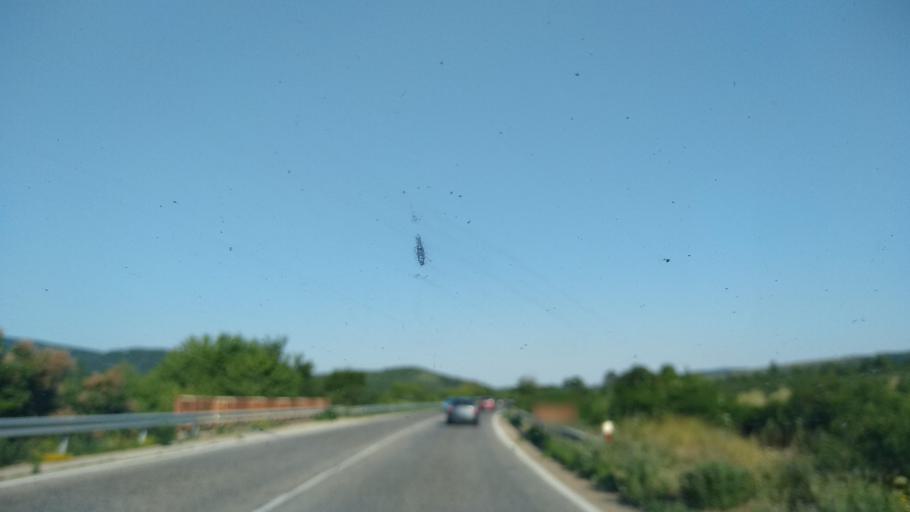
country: BG
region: Lovech
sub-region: Obshtina Lovech
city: Lovech
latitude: 43.0435
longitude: 24.8464
